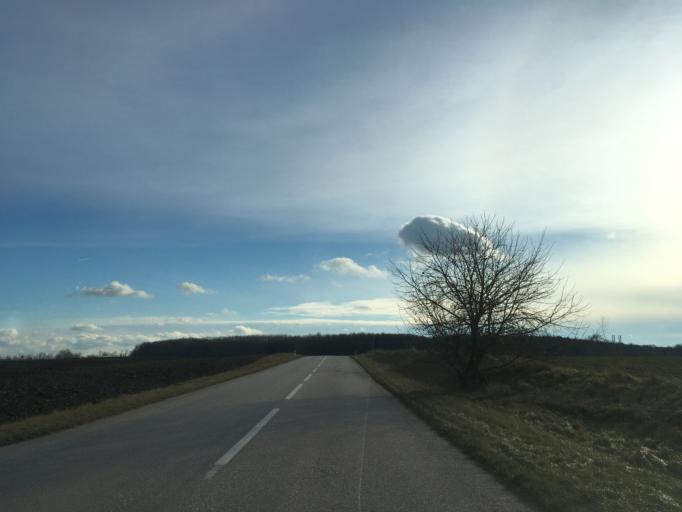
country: SK
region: Nitriansky
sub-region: Okres Komarno
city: Hurbanovo
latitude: 47.9375
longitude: 18.2422
